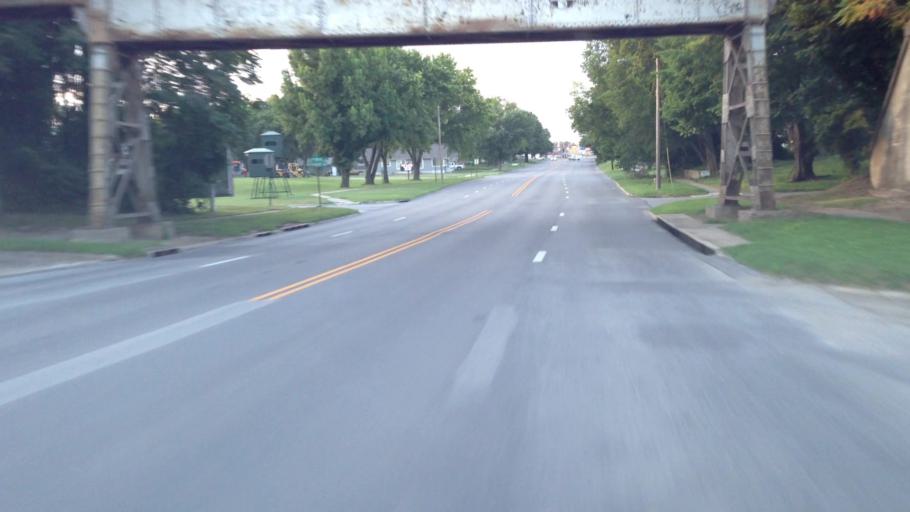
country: US
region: Kansas
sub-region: Montgomery County
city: Independence
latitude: 37.2321
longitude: -95.7065
